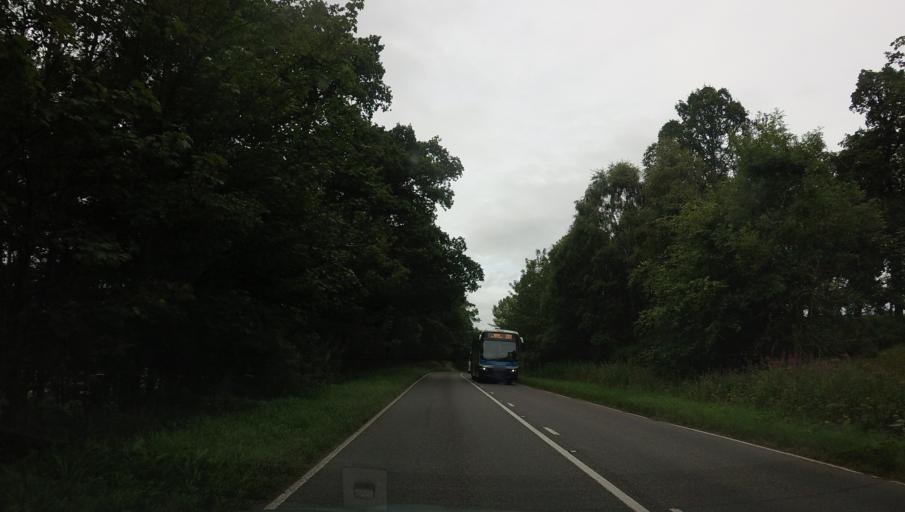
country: GB
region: Scotland
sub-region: Aberdeenshire
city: Aboyne
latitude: 57.0828
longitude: -2.7653
